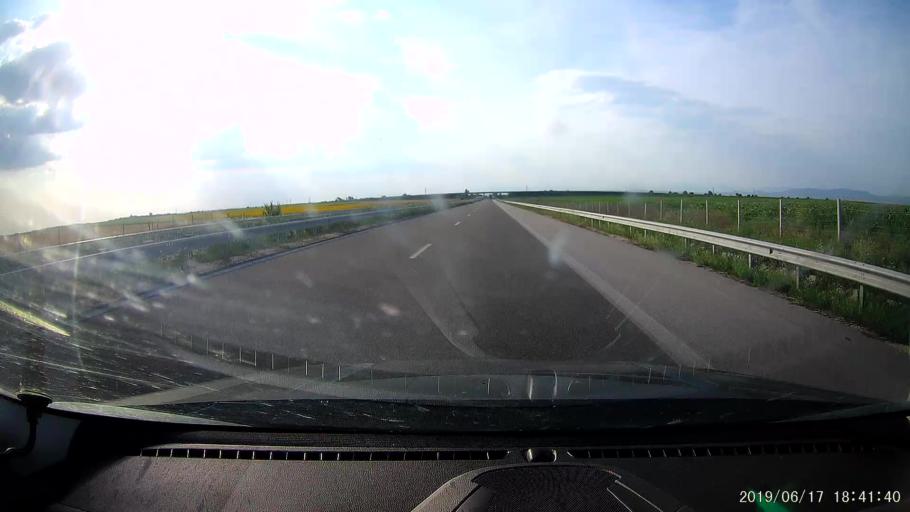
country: BG
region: Stara Zagora
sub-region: Obshtina Chirpan
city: Chirpan
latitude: 42.1767
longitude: 25.2515
